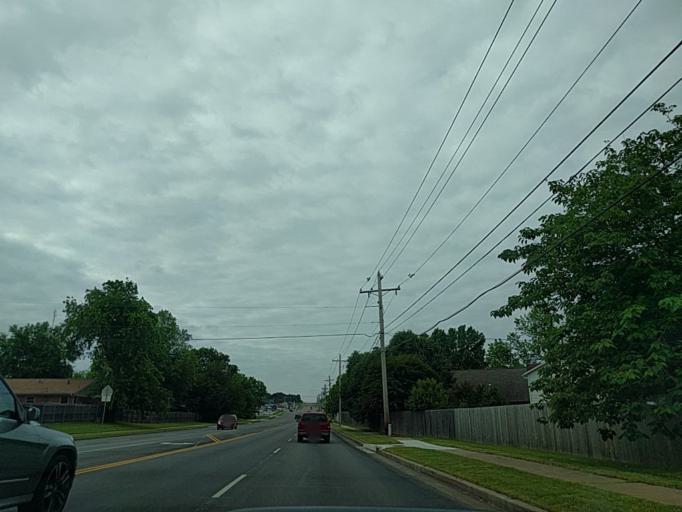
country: US
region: Oklahoma
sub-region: Tulsa County
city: Jenks
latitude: 36.0812
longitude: -95.9044
